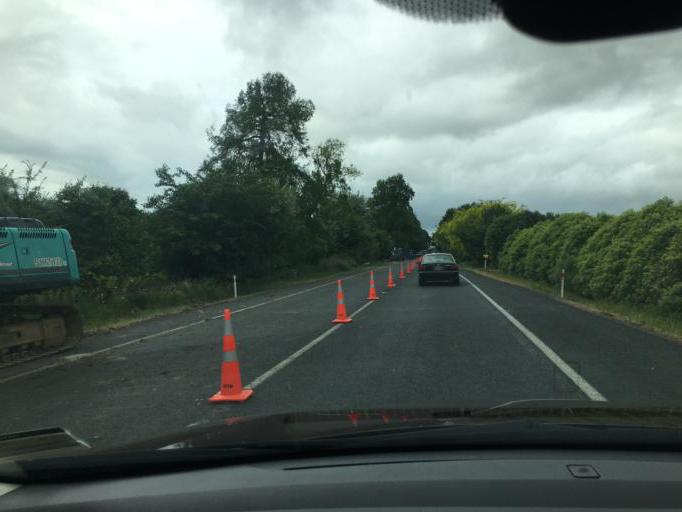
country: NZ
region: Waikato
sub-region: Waipa District
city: Cambridge
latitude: -37.9239
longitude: 175.4349
